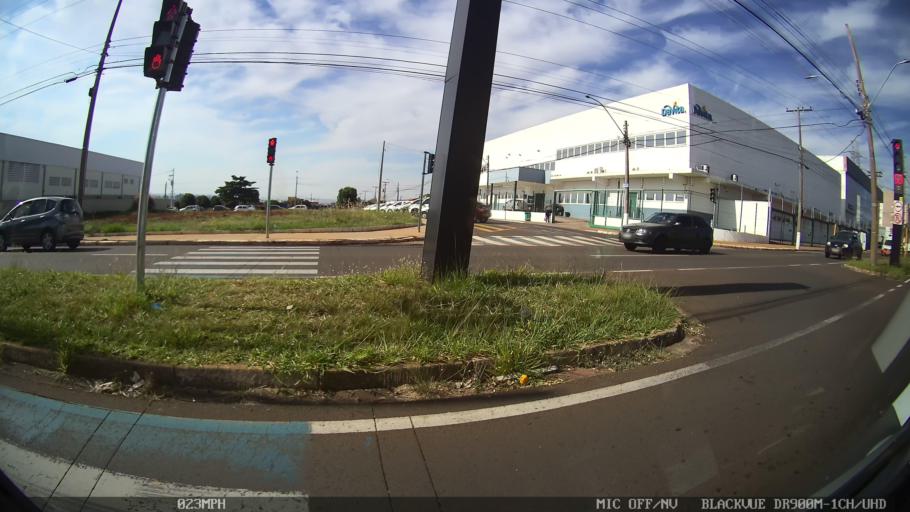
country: BR
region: Sao Paulo
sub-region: Araraquara
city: Araraquara
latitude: -21.8078
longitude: -48.1617
